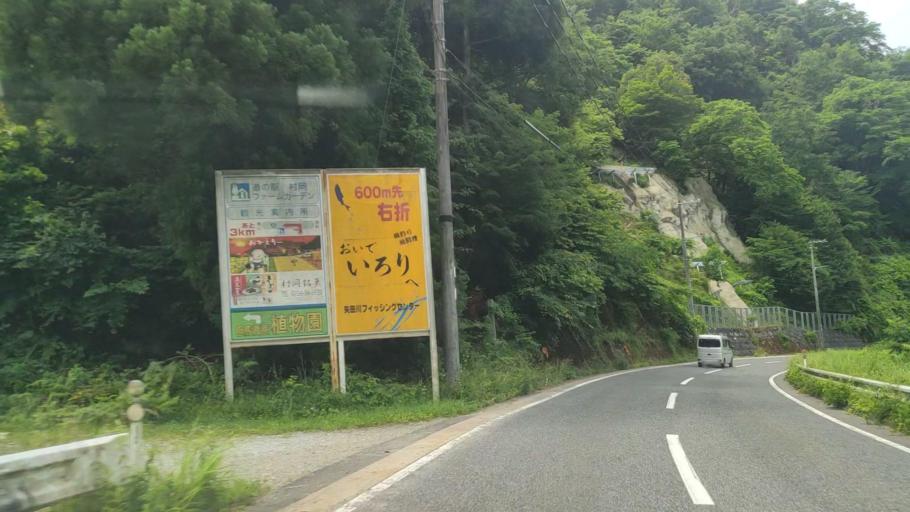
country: JP
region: Hyogo
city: Toyooka
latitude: 35.4799
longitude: 134.6124
